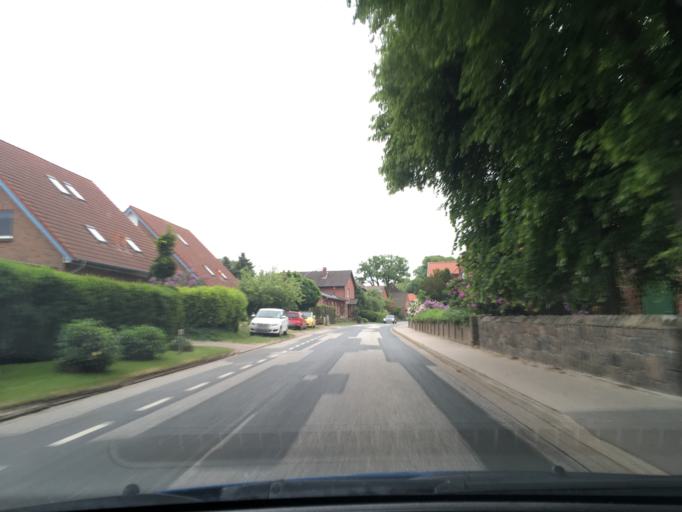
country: DE
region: Lower Saxony
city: Wulfsen
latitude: 53.3215
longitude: 10.1445
